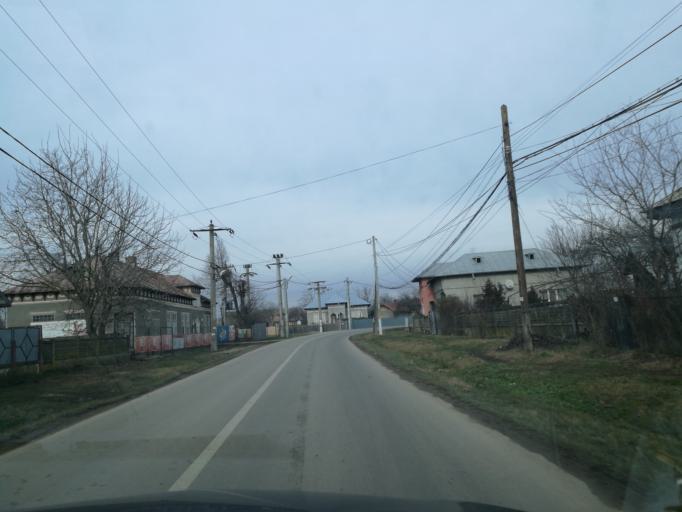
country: RO
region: Ialomita
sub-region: Comuna Fierbinti-Targ
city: Fierbintii de Jos
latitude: 44.6911
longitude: 26.3943
